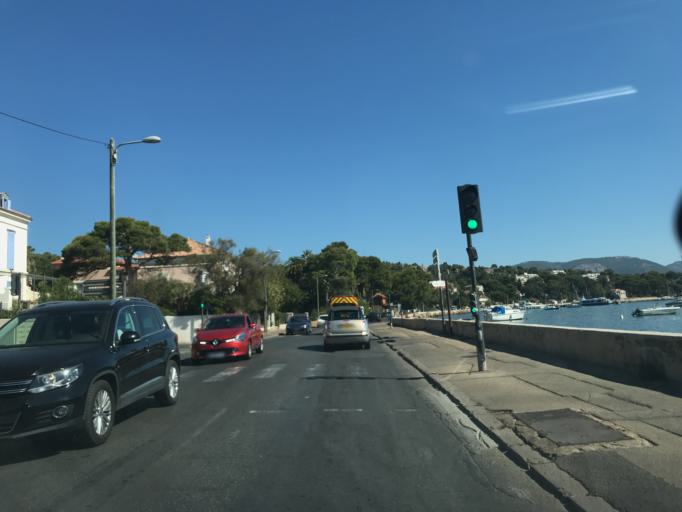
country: FR
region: Provence-Alpes-Cote d'Azur
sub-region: Departement du Var
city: La Seyne-sur-Mer
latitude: 43.0884
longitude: 5.8989
